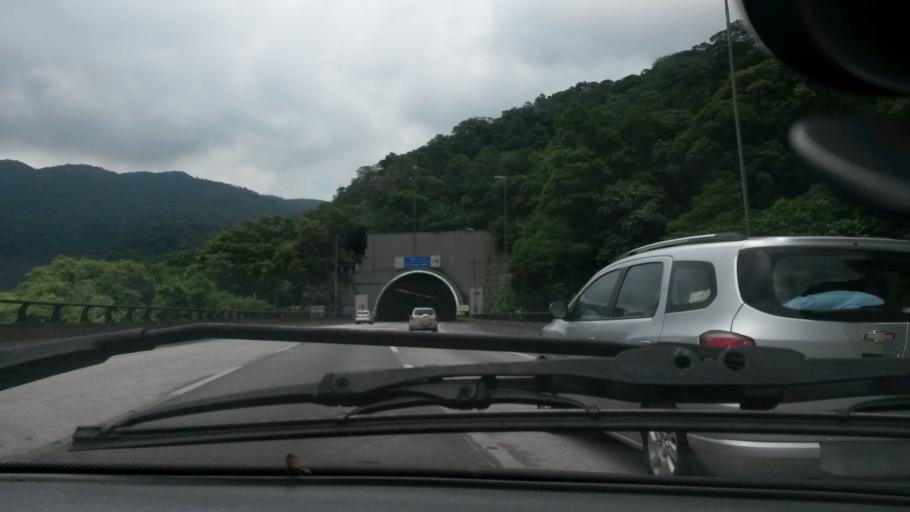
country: BR
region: Sao Paulo
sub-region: Cubatao
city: Cubatao
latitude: -23.8947
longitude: -46.4944
